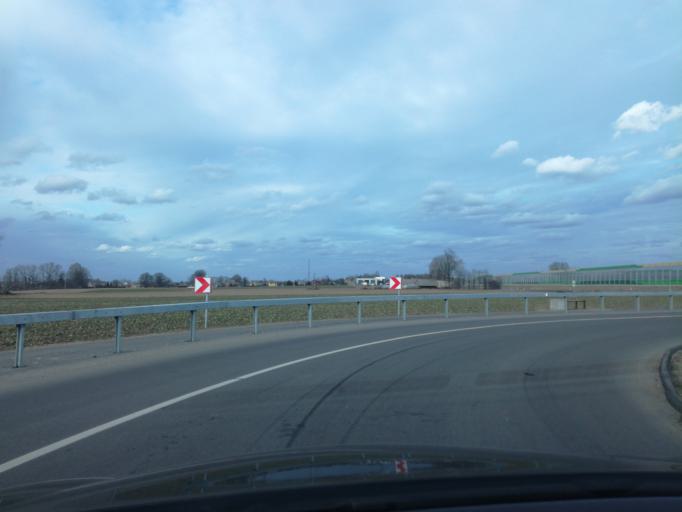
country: LT
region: Marijampoles apskritis
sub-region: Marijampole Municipality
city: Marijampole
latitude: 54.5965
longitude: 23.3934
